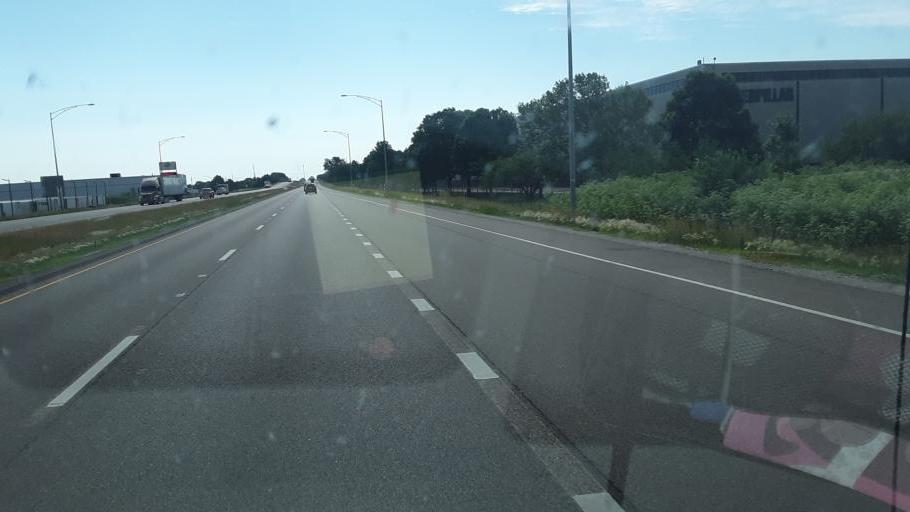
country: US
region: Illinois
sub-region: Tazewell County
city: Morton
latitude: 40.6215
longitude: -89.4582
